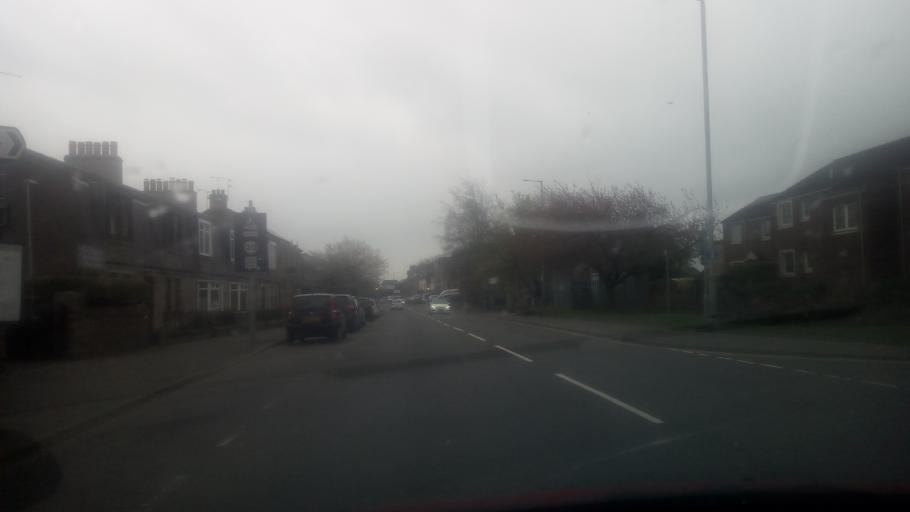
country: GB
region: Scotland
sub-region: Stirling
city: Bannockburn
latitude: 56.0898
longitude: -3.9108
